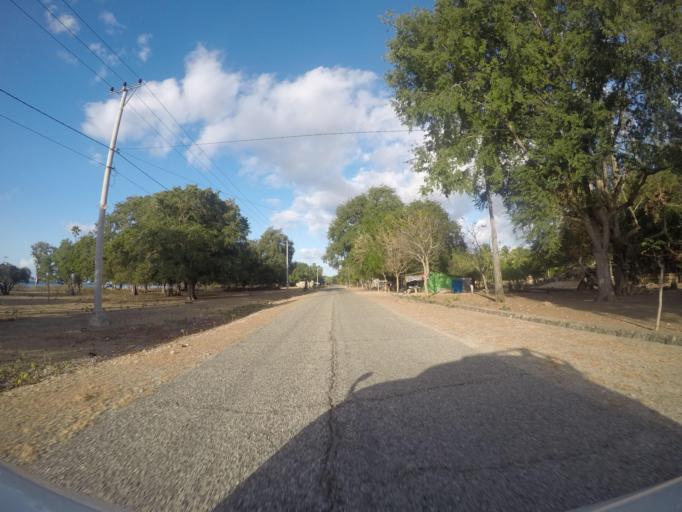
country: TL
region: Lautem
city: Lospalos
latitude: -8.3358
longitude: 126.9468
